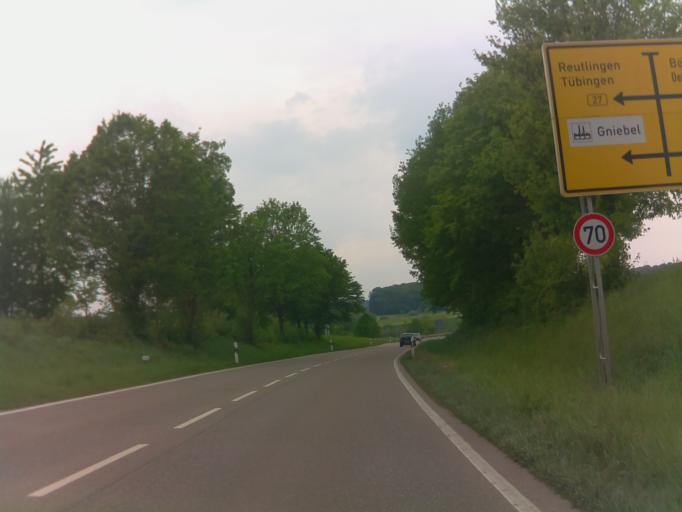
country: DE
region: Baden-Wuerttemberg
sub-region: Tuebingen Region
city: Pliezhausen
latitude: 48.5802
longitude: 9.1784
